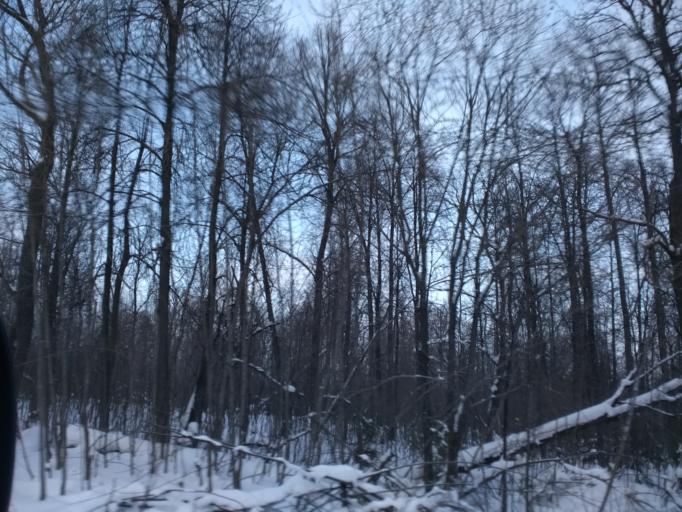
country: RU
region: Bashkortostan
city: Kudeyevskiy
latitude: 54.7198
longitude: 56.6074
